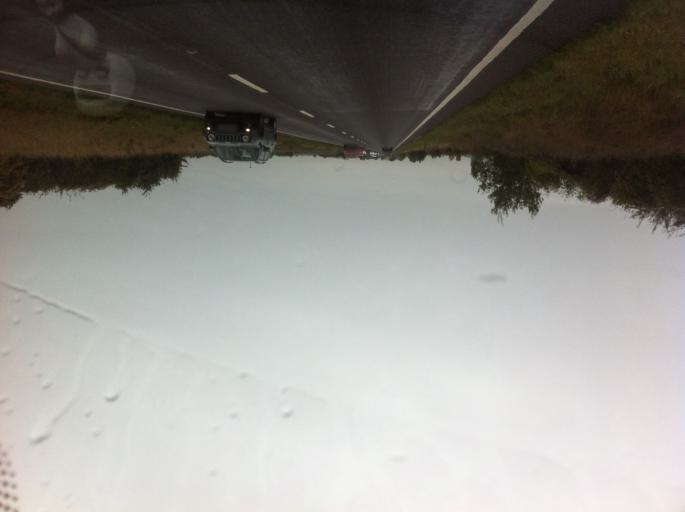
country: GB
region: England
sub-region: Peterborough
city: Eye
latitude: 52.6186
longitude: -0.2066
